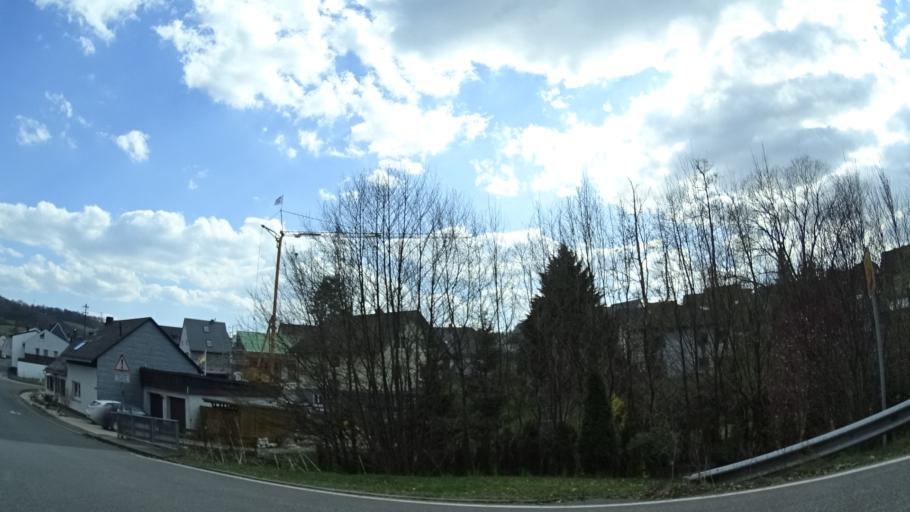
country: DE
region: Rheinland-Pfalz
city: Niederworresbach
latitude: 49.7708
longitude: 7.3320
